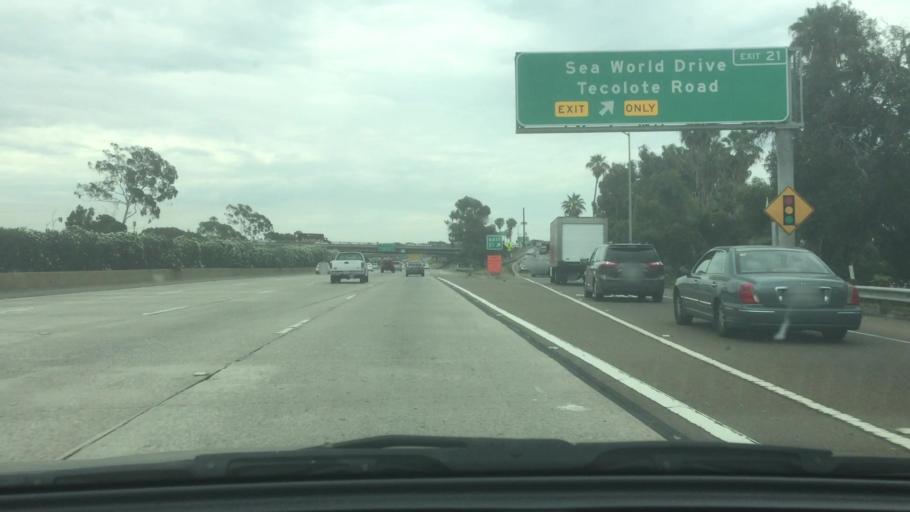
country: US
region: California
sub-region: San Diego County
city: San Diego
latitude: 32.7725
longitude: -117.2075
